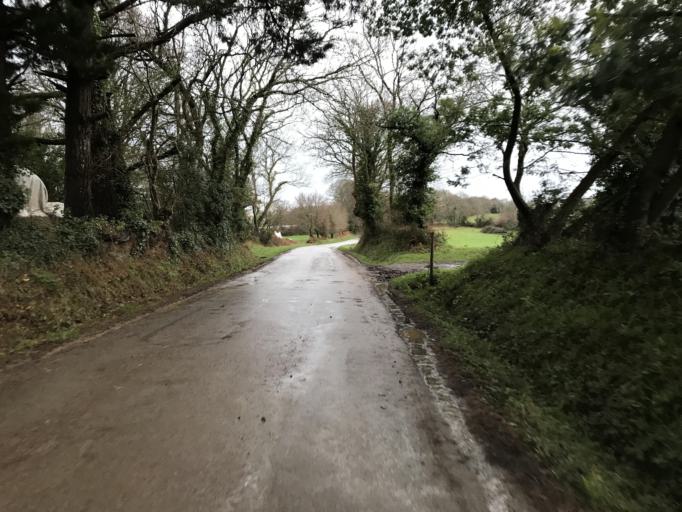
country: FR
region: Brittany
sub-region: Departement du Finistere
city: Loperhet
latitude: 48.3660
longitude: -4.3245
